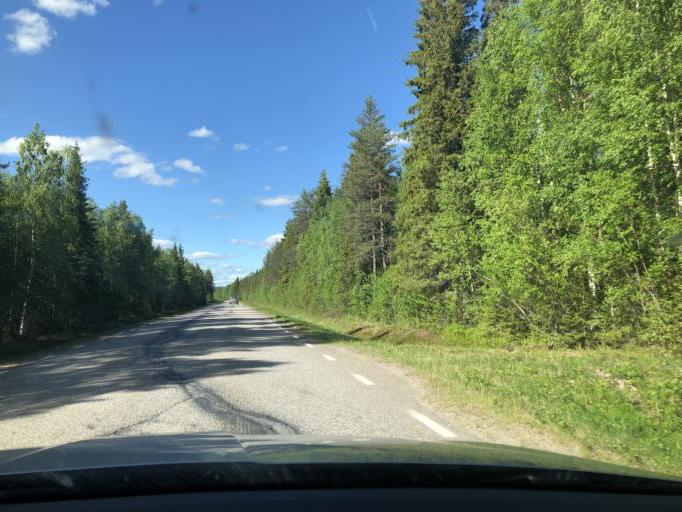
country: SE
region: Norrbotten
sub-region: Kalix Kommun
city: Kalix
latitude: 65.9599
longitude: 23.1487
